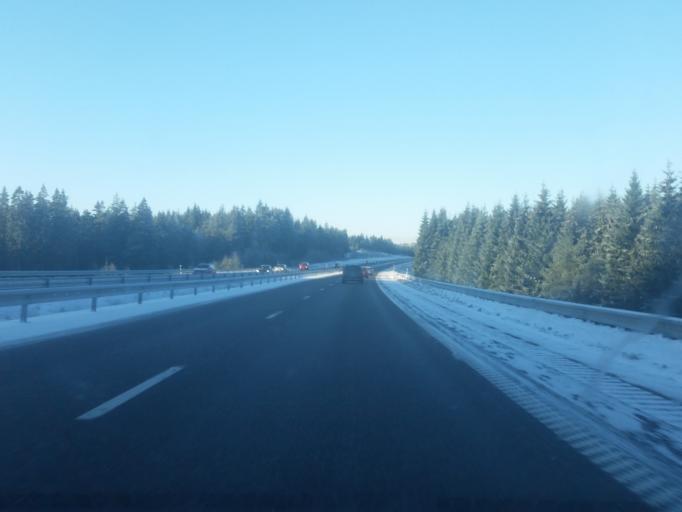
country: SE
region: Vaestra Goetaland
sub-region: Harryda Kommun
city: Hindas
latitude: 57.6670
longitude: 12.4040
